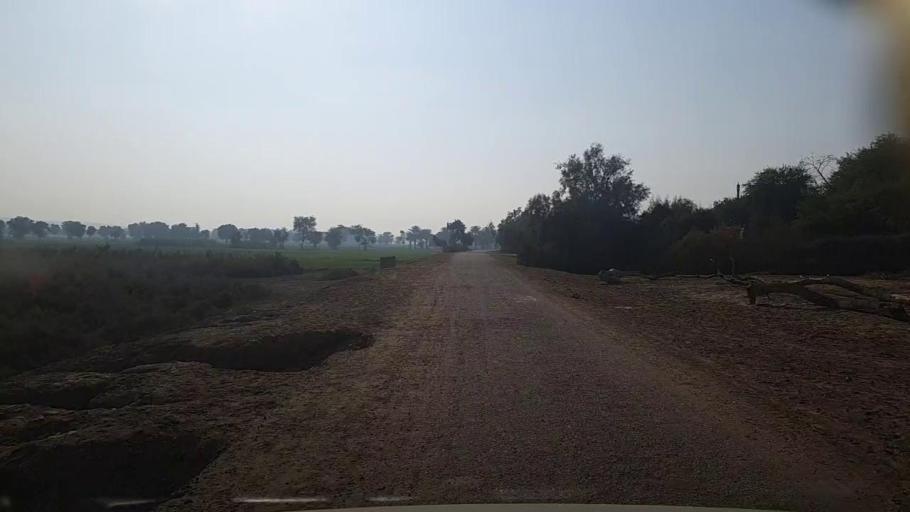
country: PK
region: Sindh
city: Karaundi
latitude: 26.7886
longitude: 68.4729
